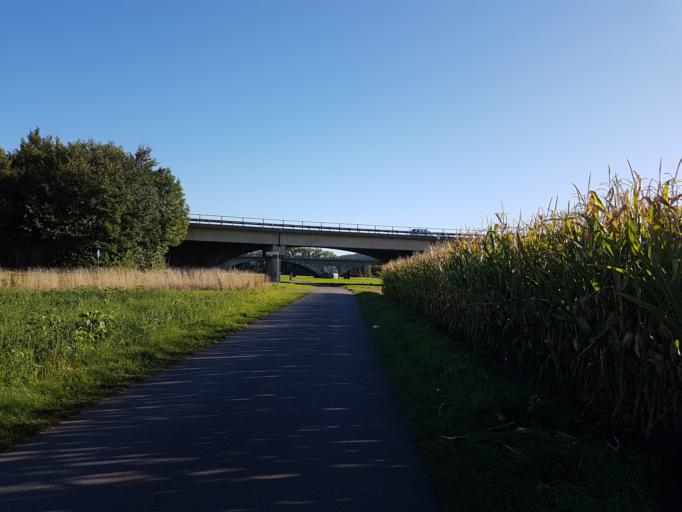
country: DE
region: North Rhine-Westphalia
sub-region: Regierungsbezirk Detmold
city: Vlotho
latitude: 52.2079
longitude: 8.8482
